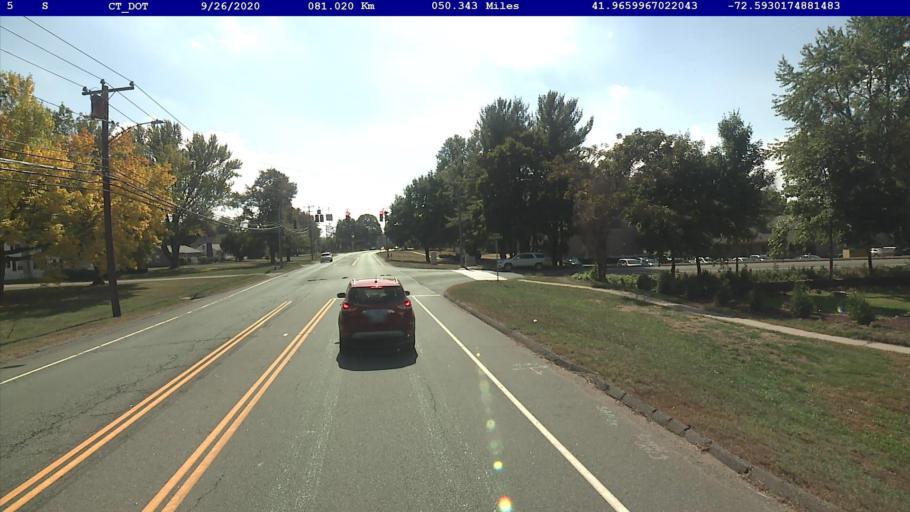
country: US
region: Connecticut
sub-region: Hartford County
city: Enfield
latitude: 41.9661
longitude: -72.5930
